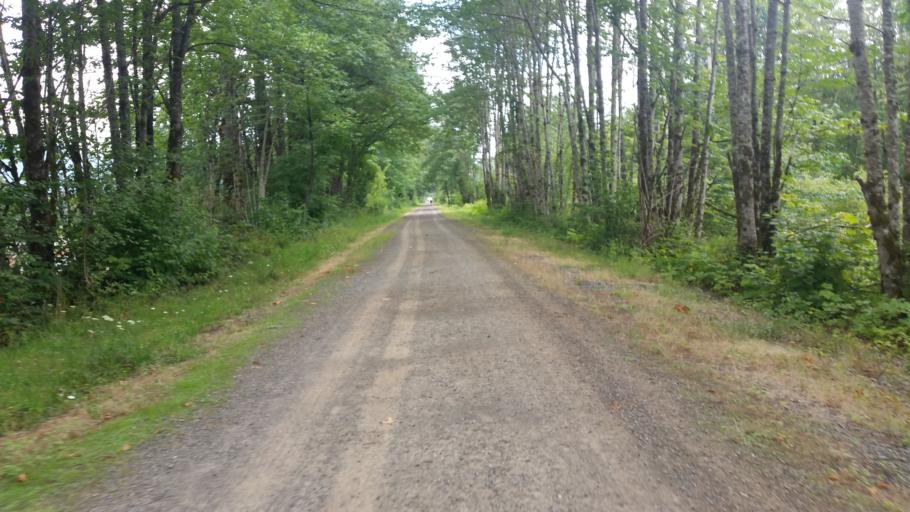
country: US
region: Washington
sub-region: King County
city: Snoqualmie
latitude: 47.5281
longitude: -121.8056
